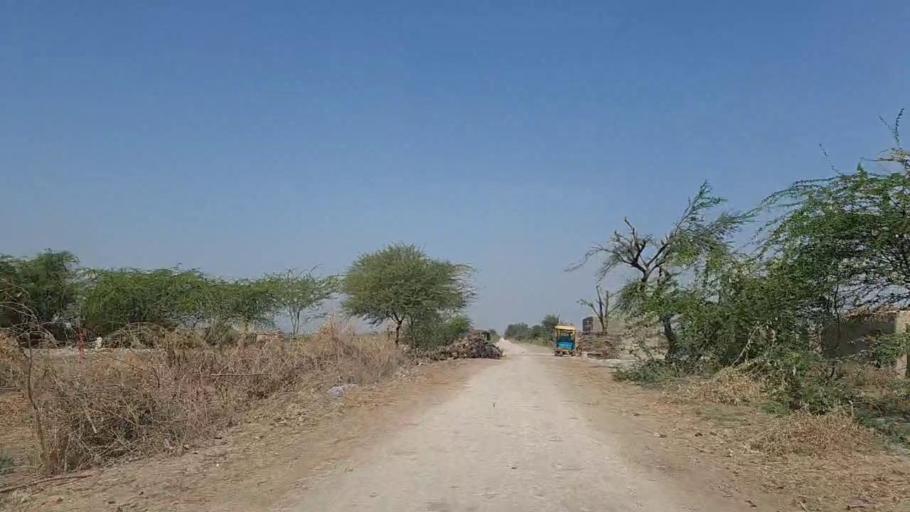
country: PK
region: Sindh
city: Samaro
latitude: 25.1976
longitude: 69.4041
